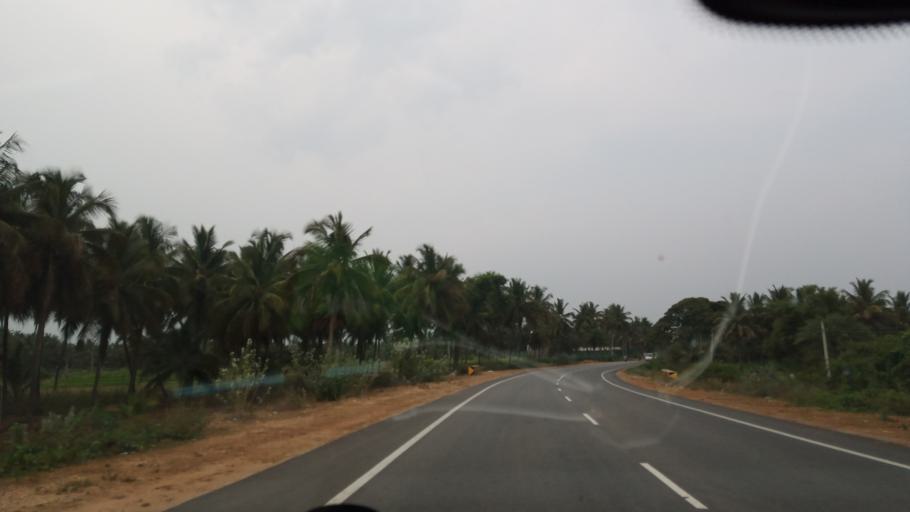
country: IN
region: Karnataka
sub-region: Mandya
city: Nagamangala
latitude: 12.7576
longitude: 76.7320
